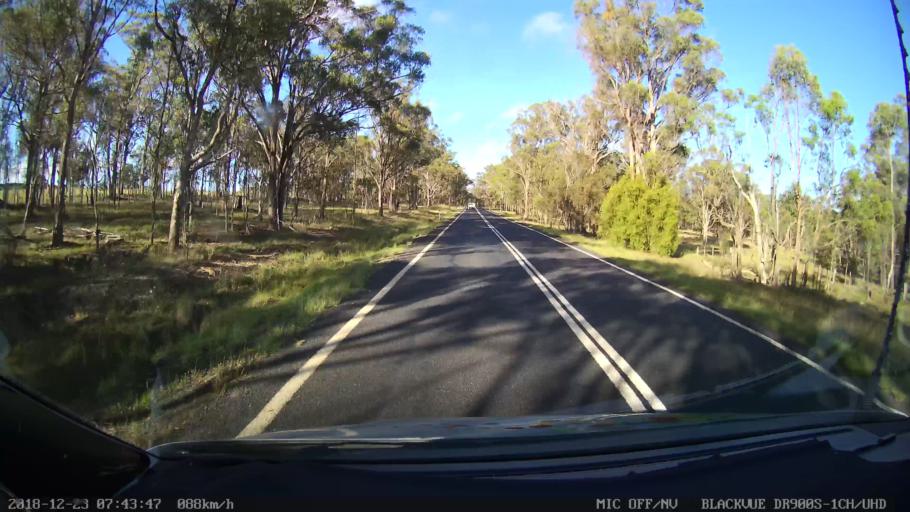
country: AU
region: New South Wales
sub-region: Armidale Dumaresq
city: Enmore
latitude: -30.5245
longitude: 151.9599
